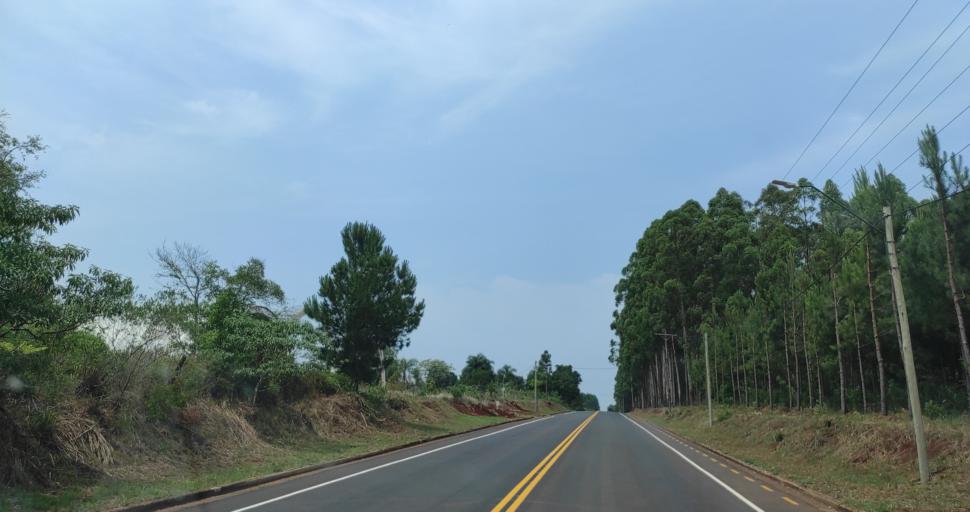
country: AR
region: Misiones
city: Capiovi
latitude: -26.9443
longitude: -55.0546
